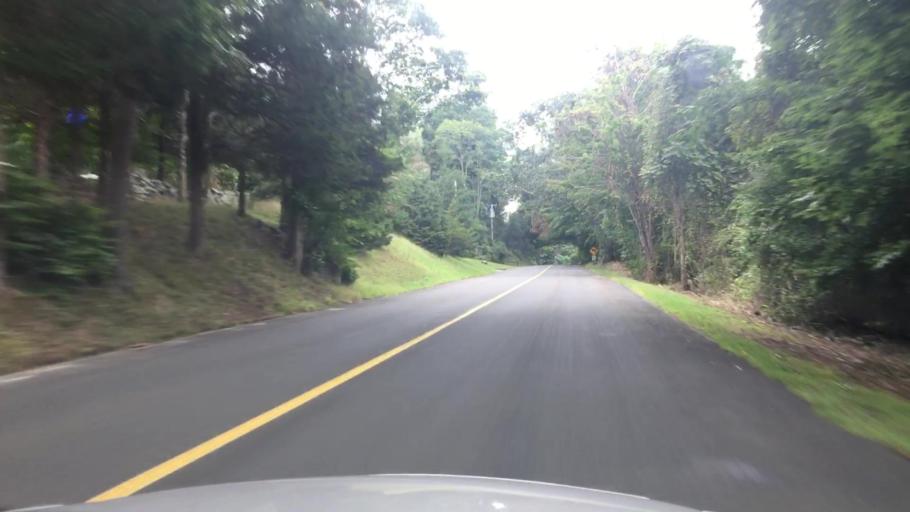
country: US
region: Connecticut
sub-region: Middlesex County
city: Essex Village
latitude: 41.3731
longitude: -72.3906
